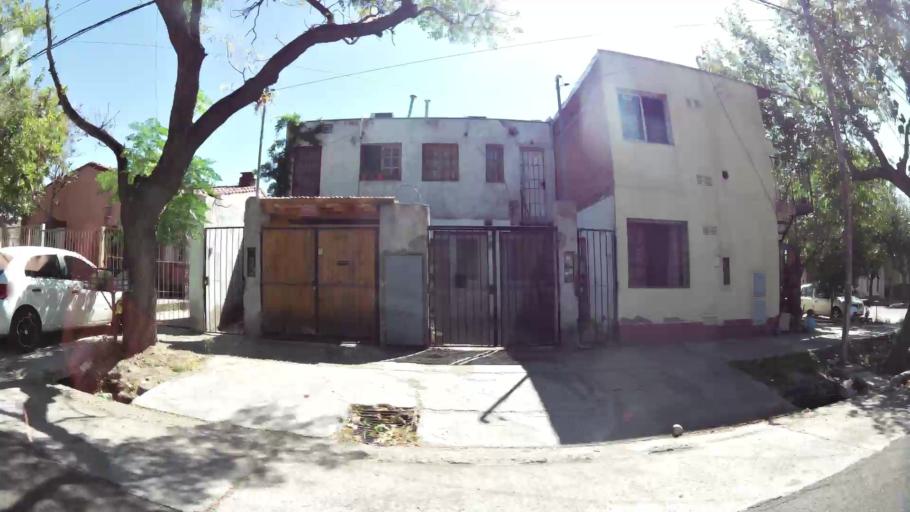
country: AR
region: Mendoza
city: Villa Nueva
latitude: -32.8987
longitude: -68.7938
